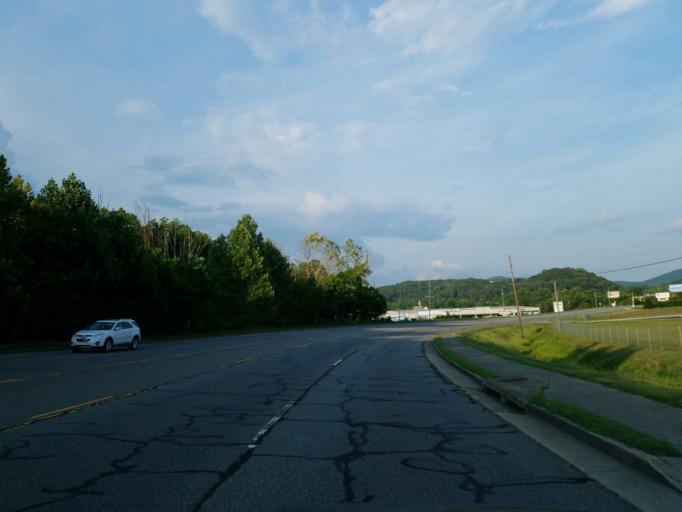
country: US
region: Georgia
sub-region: Gilmer County
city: Ellijay
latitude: 34.6861
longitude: -84.4885
